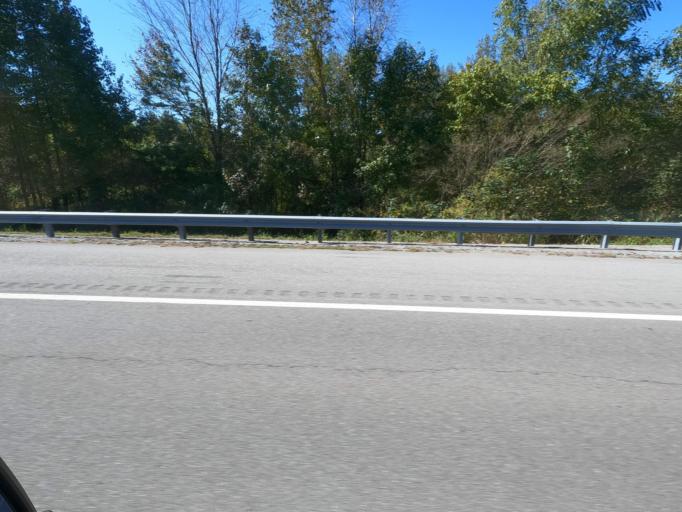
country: US
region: Tennessee
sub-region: Maury County
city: Mount Pleasant
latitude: 35.4206
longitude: -87.2824
